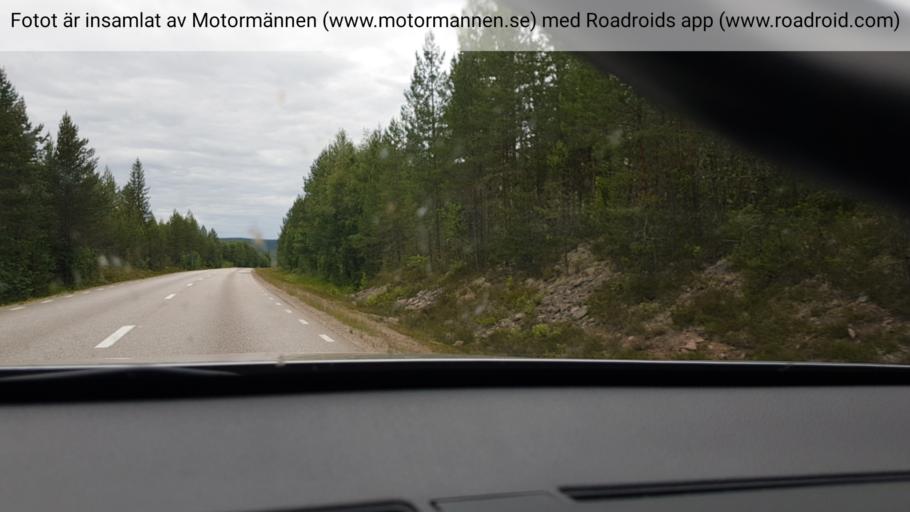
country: NO
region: Hedmark
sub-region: Trysil
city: Innbygda
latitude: 60.9319
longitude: 12.4944
